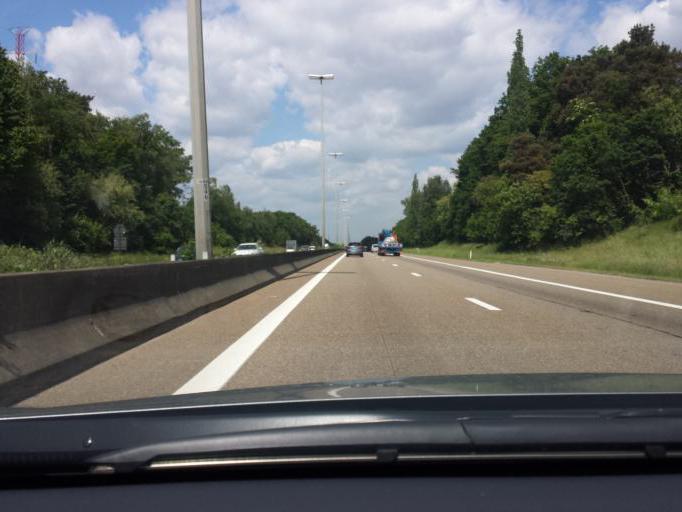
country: BE
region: Flanders
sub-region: Provincie Limburg
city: Lummen
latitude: 51.0105
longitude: 5.2152
